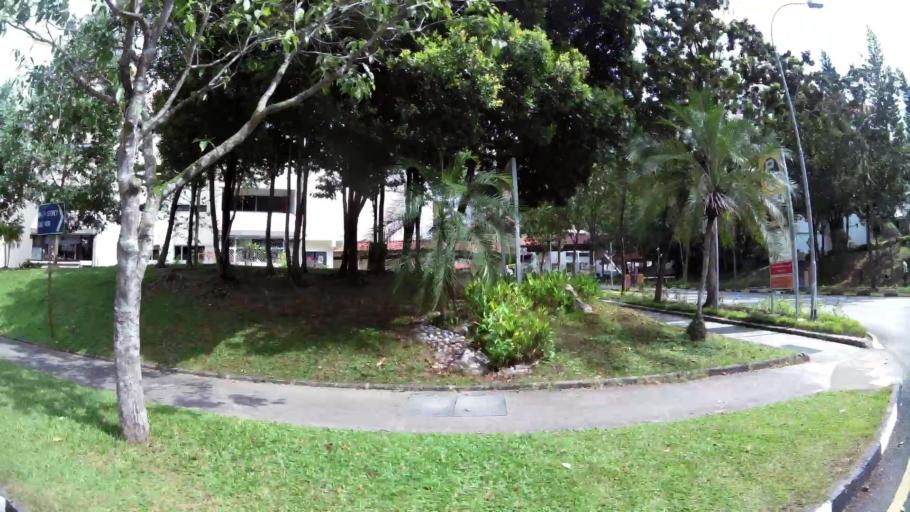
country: SG
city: Singapore
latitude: 1.3229
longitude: 103.7702
